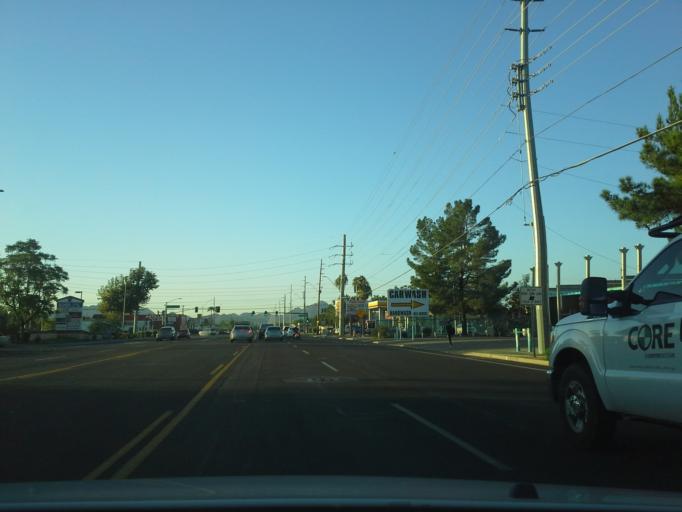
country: US
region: Arizona
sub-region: Maricopa County
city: Paradise Valley
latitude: 33.6284
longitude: -112.0135
